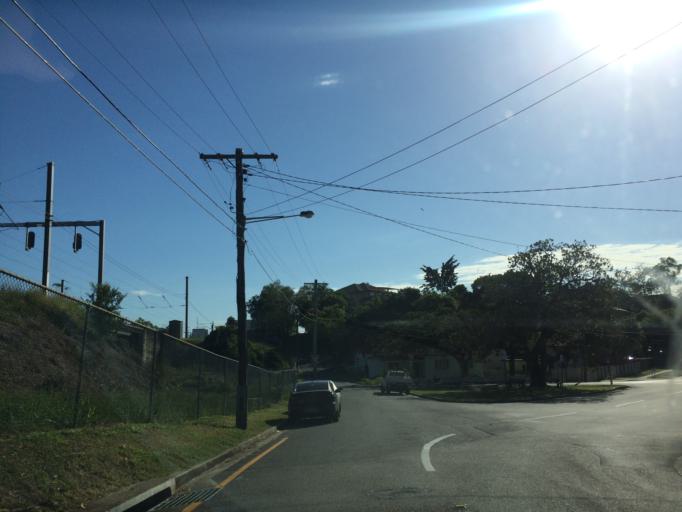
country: AU
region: Queensland
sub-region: Brisbane
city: Taringa
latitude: -27.4927
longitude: 152.9834
